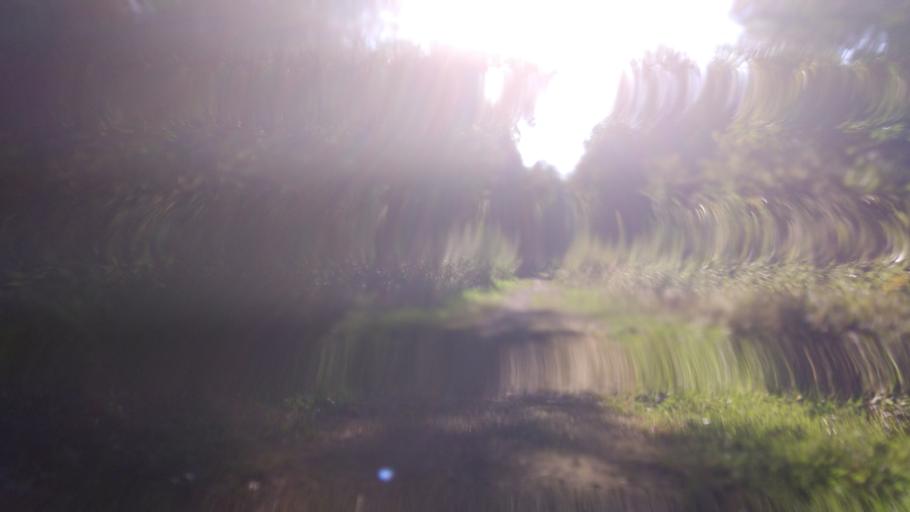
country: FR
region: Alsace
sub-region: Departement du Bas-Rhin
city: Bischwiller
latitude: 48.7604
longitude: 7.8385
